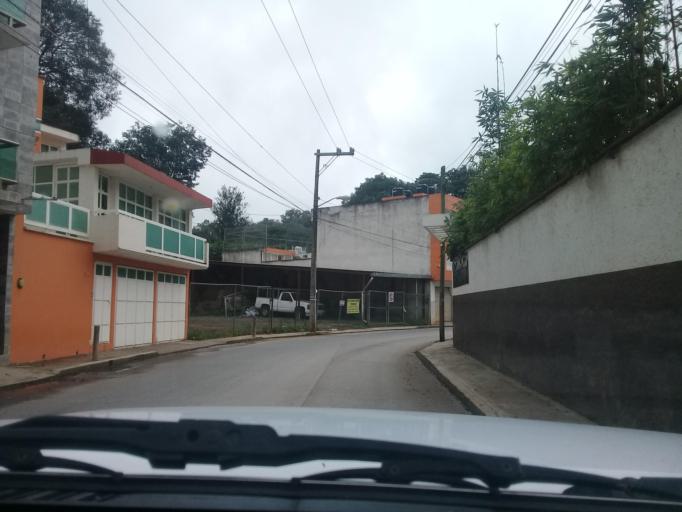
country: MX
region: Veracruz
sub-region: Xalapa
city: Lomas Verdes
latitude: 19.5095
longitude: -96.9071
